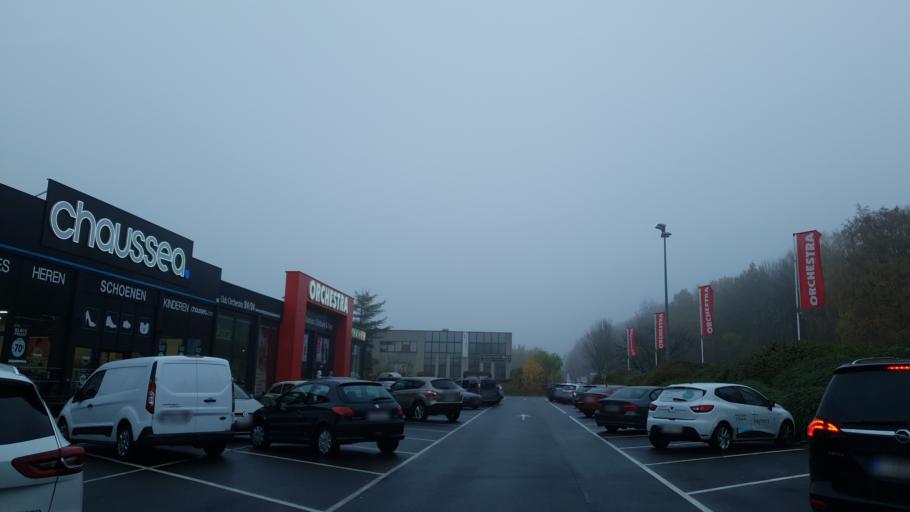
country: BE
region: Flanders
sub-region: Provincie Vlaams-Brabant
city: Wezembeek-Oppem
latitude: 50.8702
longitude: 4.5050
